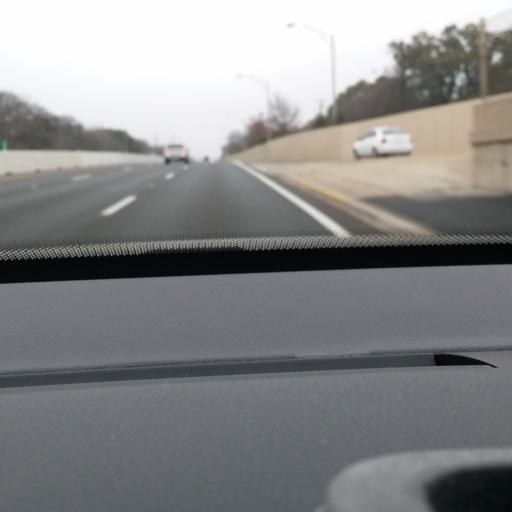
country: US
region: Texas
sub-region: Dallas County
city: University Park
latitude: 32.8737
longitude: -96.7988
